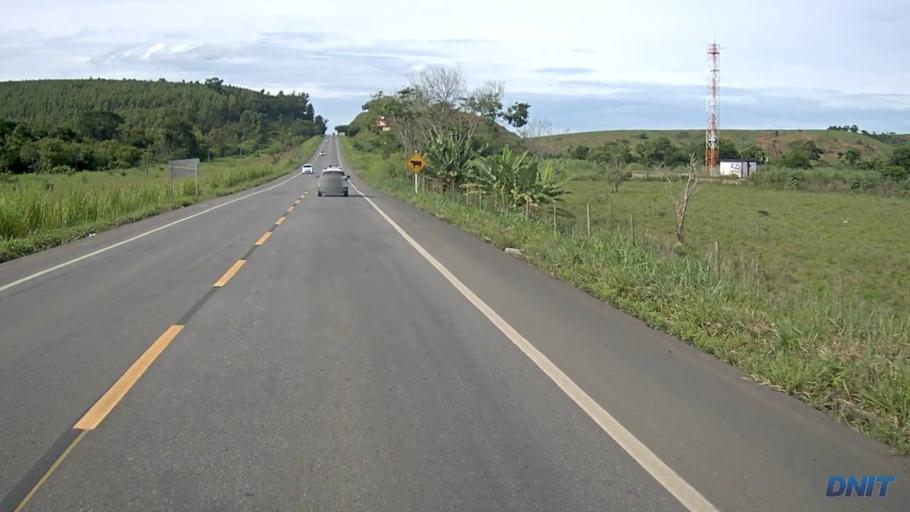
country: BR
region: Minas Gerais
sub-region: Belo Oriente
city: Belo Oriente
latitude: -19.2574
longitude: -42.3419
